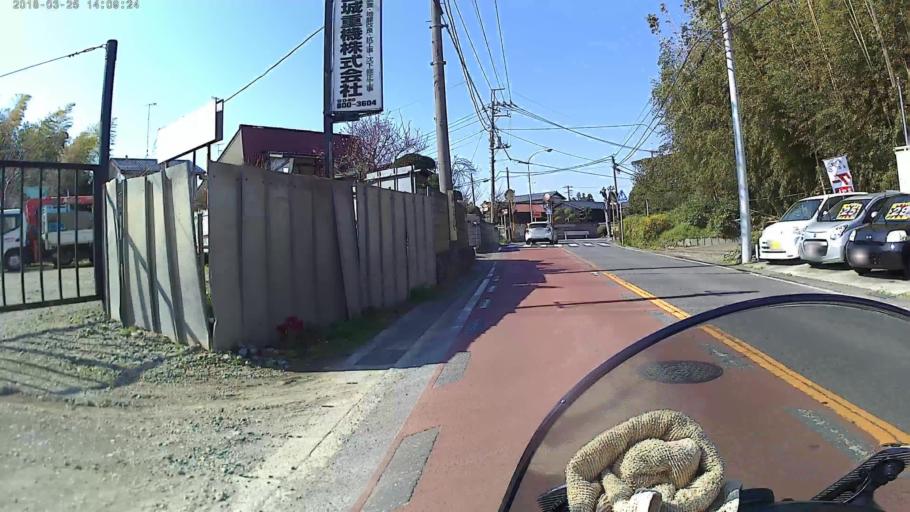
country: JP
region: Kanagawa
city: Minami-rinkan
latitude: 35.4242
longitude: 139.4757
